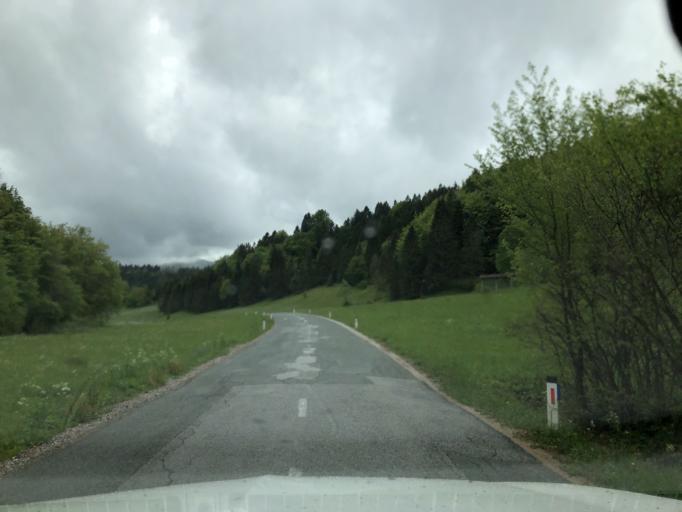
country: SI
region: Gorje
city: Zgornje Gorje
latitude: 46.4005
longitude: 14.0745
